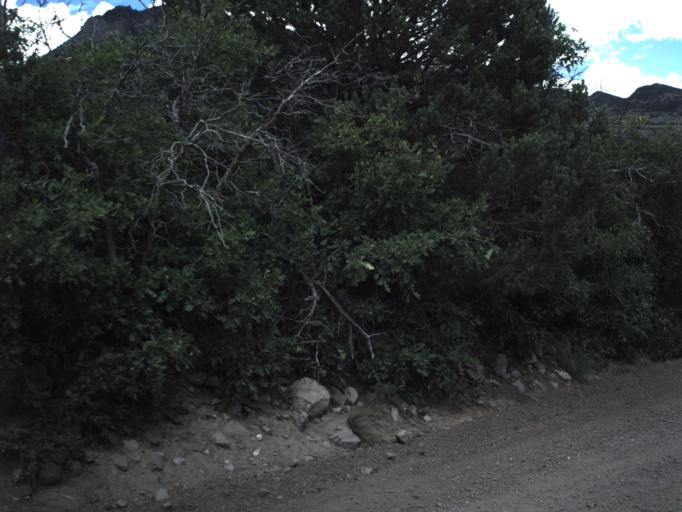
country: US
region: Utah
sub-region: Piute County
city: Junction
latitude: 38.2639
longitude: -112.3057
